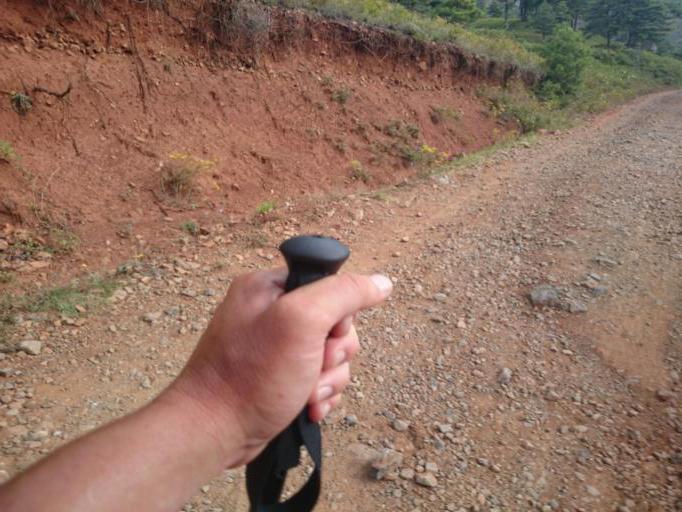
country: AL
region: Elbasan
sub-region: Rrethi i Gramshit
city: Lenias
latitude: 40.7751
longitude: 20.3491
